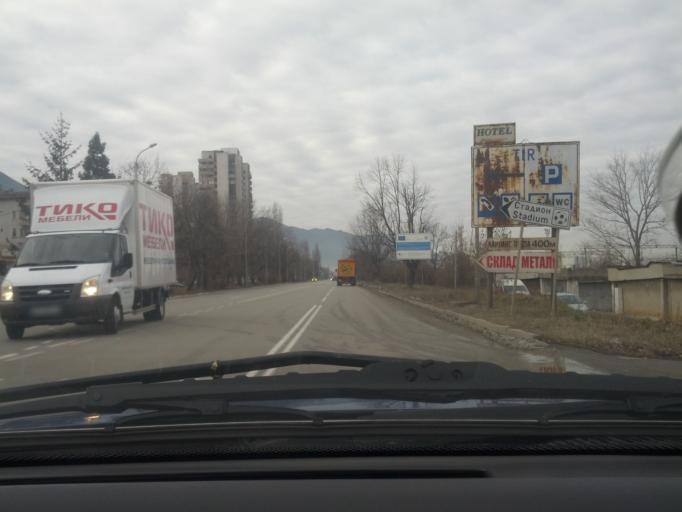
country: BG
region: Vratsa
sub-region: Obshtina Vratsa
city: Vratsa
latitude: 43.2058
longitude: 23.5672
